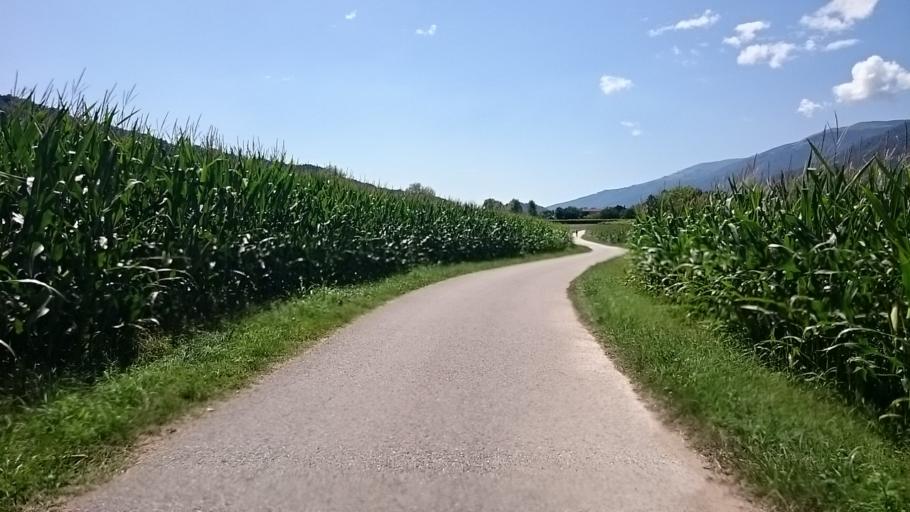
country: IT
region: Veneto
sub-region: Provincia di Treviso
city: Cison di Valmarino
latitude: 45.9641
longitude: 12.1545
